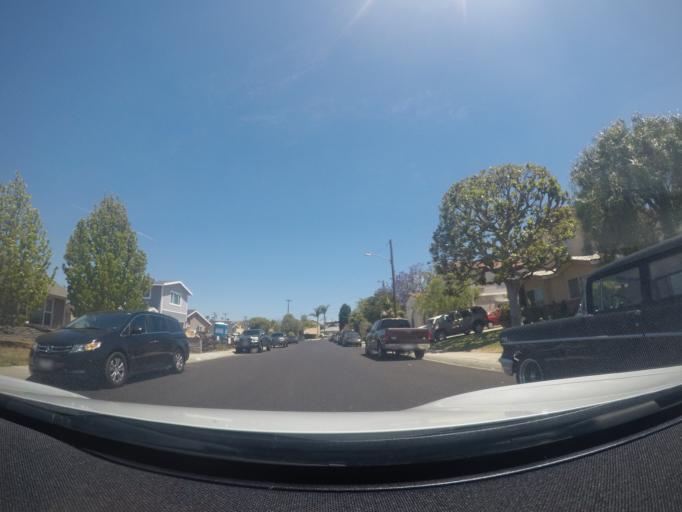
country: US
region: California
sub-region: Los Angeles County
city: Rolling Hills Estates
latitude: 33.7987
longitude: -118.3426
